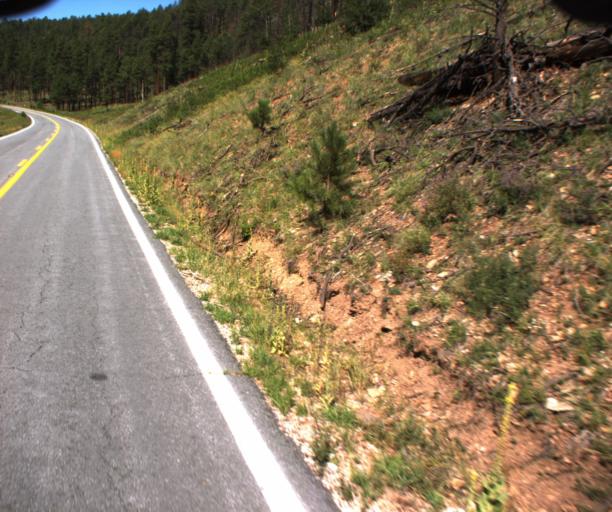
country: US
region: Arizona
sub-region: Apache County
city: Eagar
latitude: 33.7916
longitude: -109.1620
